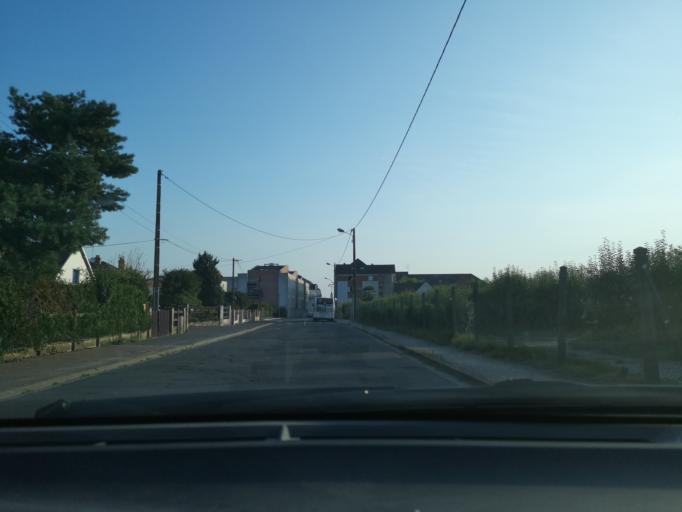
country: FR
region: Centre
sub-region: Departement du Loiret
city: Fleury-les-Aubrais
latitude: 47.9379
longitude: 1.9300
